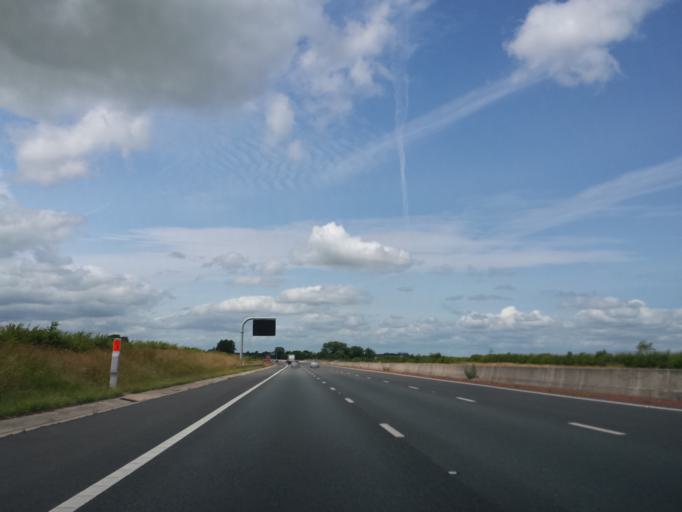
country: GB
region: England
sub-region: North Yorkshire
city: Bedale
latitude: 54.2422
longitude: -1.5008
